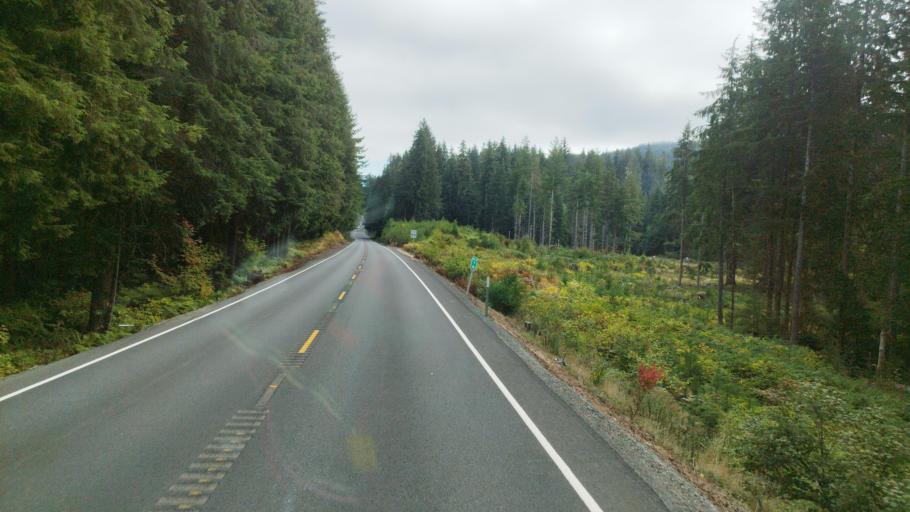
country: US
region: Oregon
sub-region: Clatsop County
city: Seaside
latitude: 45.8960
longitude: -123.6482
